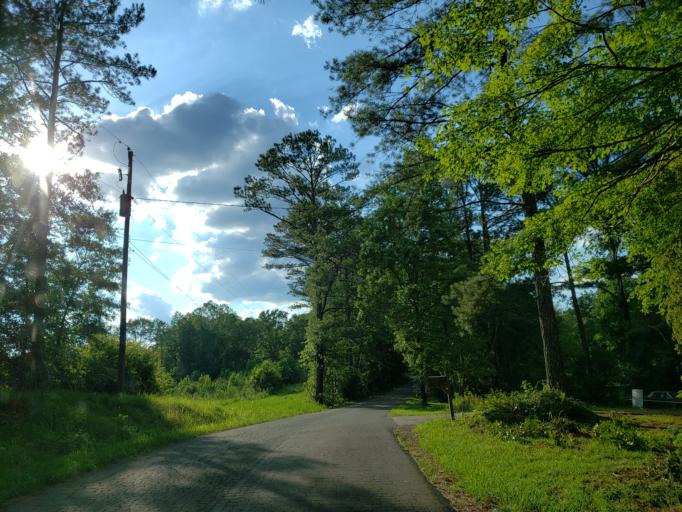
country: US
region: Georgia
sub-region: Haralson County
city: Buchanan
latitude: 33.9003
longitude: -85.2576
